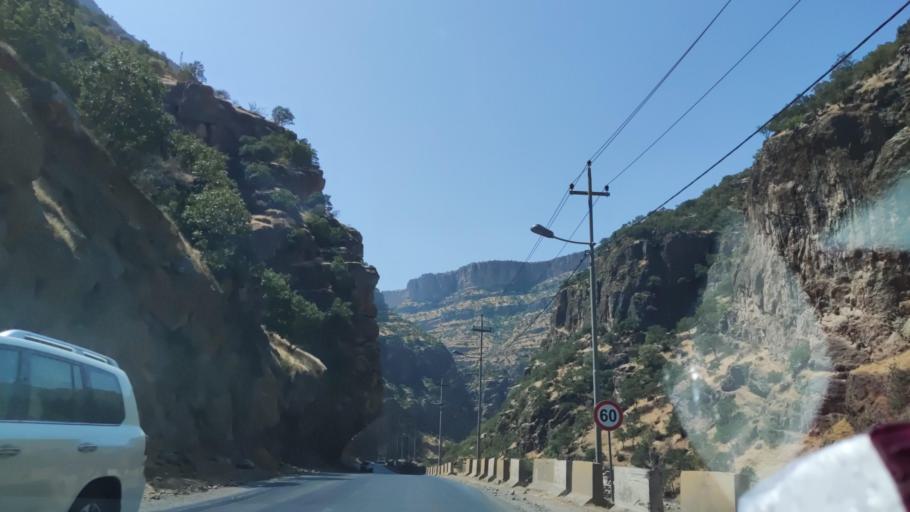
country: IQ
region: Arbil
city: Ruwandiz
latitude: 36.6394
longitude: 44.4920
